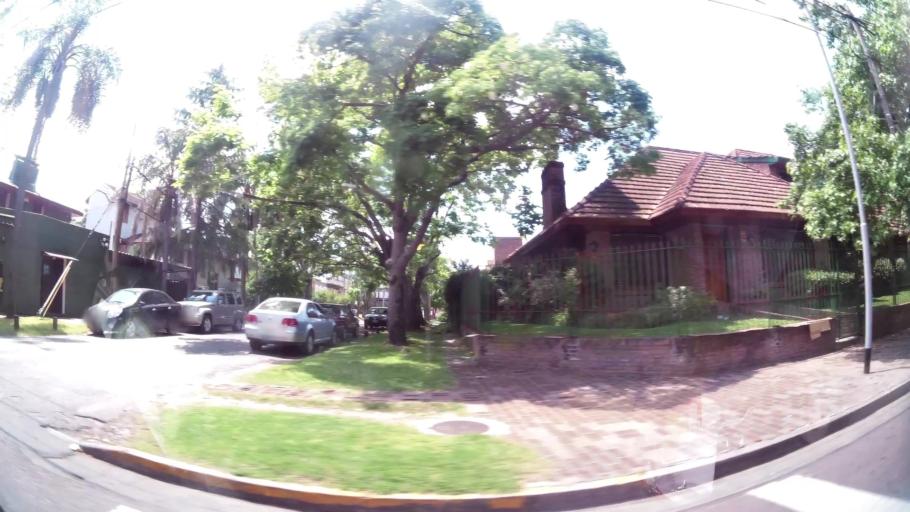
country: AR
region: Buenos Aires
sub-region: Partido de Tigre
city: Tigre
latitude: -34.4143
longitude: -58.5909
